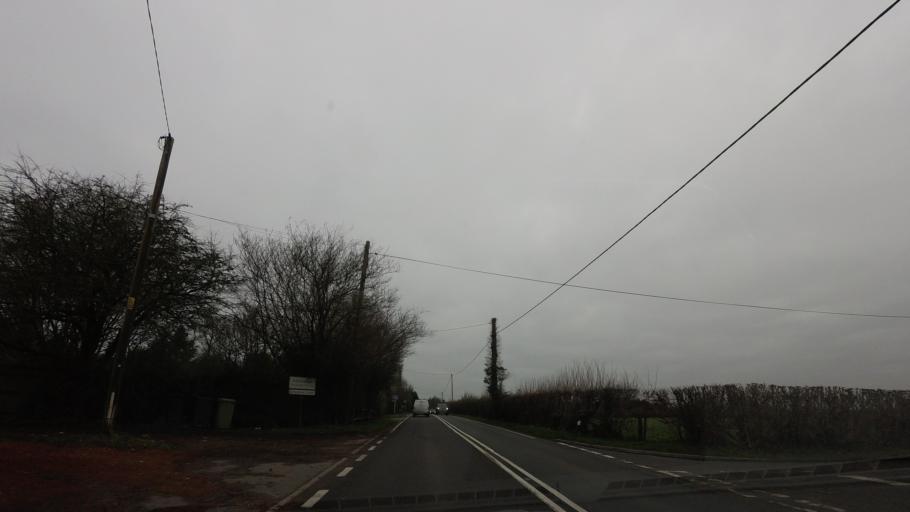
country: GB
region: England
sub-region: East Sussex
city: Saint Leonards-on-Sea
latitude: 50.9099
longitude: 0.5456
